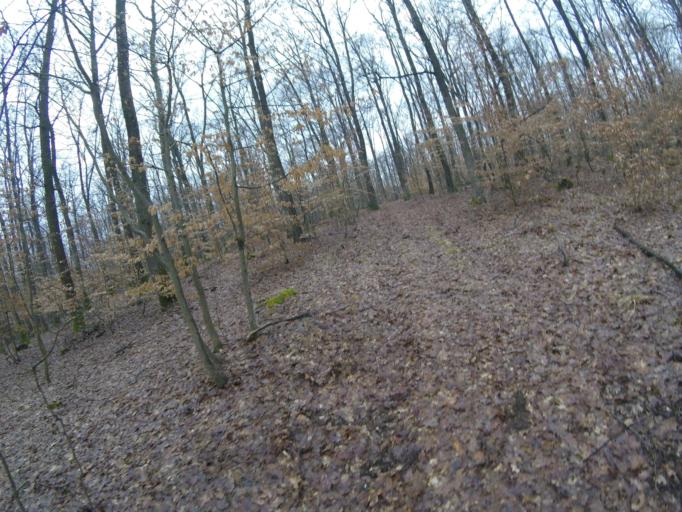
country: HU
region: Borsod-Abauj-Zemplen
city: Rudabanya
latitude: 48.4510
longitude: 20.5748
